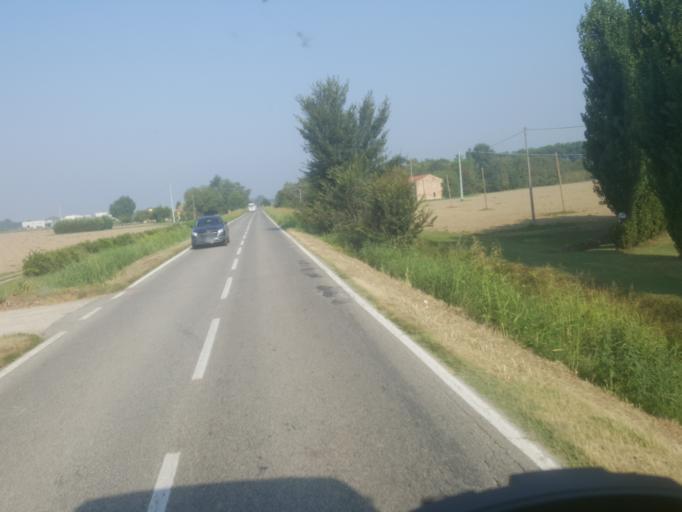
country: IT
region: Emilia-Romagna
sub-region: Provincia di Ravenna
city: Lavezzola
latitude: 44.5661
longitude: 11.8978
